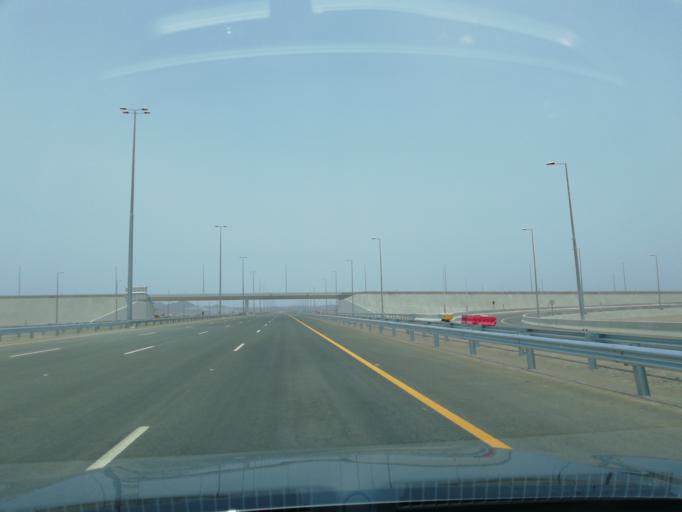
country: OM
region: Al Batinah
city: Al Liwa'
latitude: 24.4559
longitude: 56.5151
